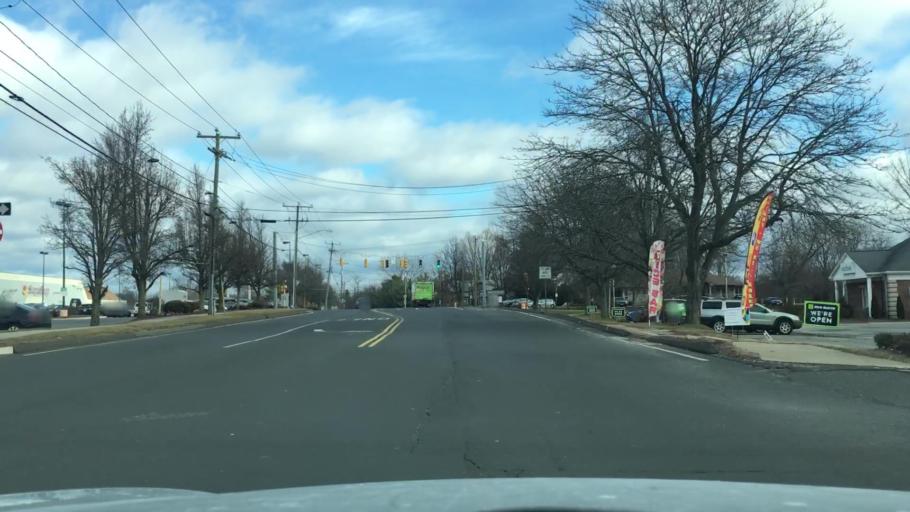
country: US
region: Massachusetts
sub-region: Hampden County
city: Agawam
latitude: 42.0671
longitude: -72.6764
